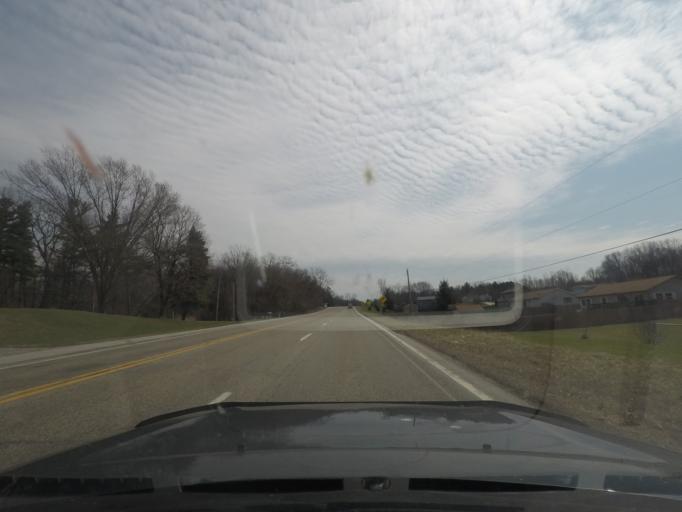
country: US
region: Indiana
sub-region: LaPorte County
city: LaPorte
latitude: 41.6666
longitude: -86.7748
